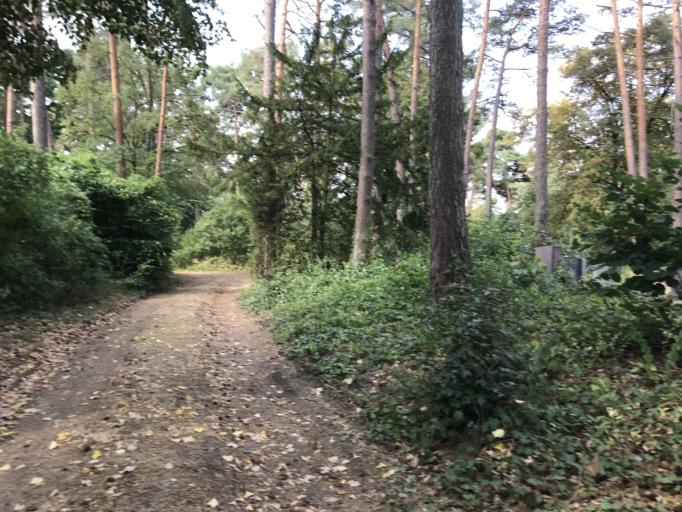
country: DE
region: Rheinland-Pfalz
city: Budenheim
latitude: 50.0206
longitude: 8.1973
